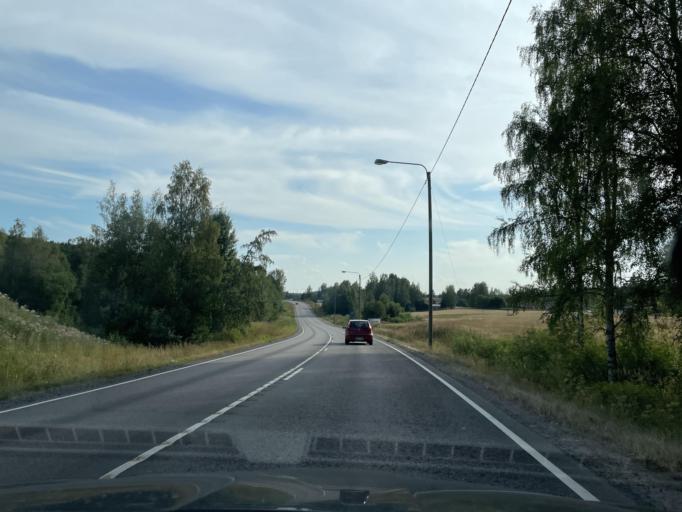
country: FI
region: Central Finland
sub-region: Jaemsae
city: Kuhmoinen
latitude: 61.5764
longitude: 25.1845
